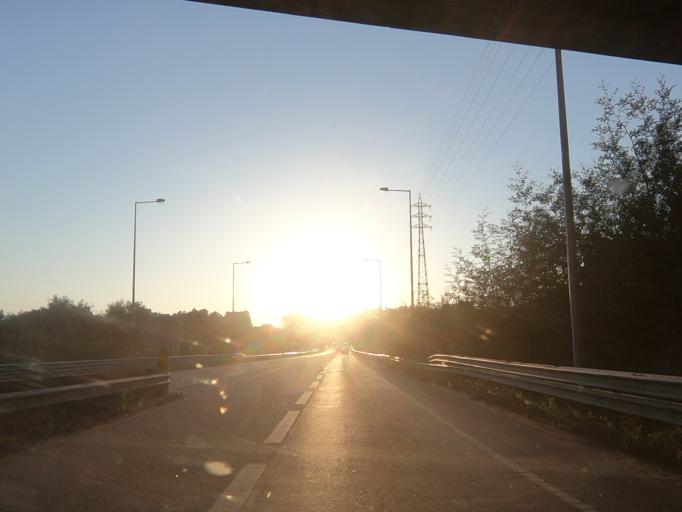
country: PT
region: Viseu
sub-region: Viseu
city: Rio de Loba
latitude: 40.6809
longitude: -7.8828
